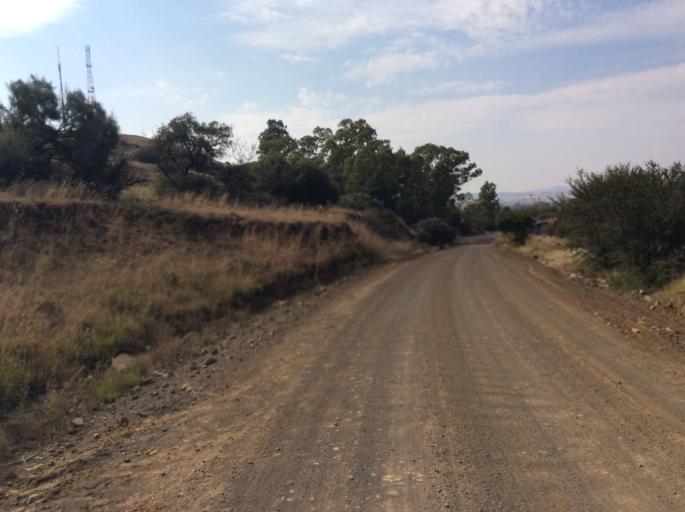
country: ZA
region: Orange Free State
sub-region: Xhariep District Municipality
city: Dewetsdorp
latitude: -29.5831
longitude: 26.6579
